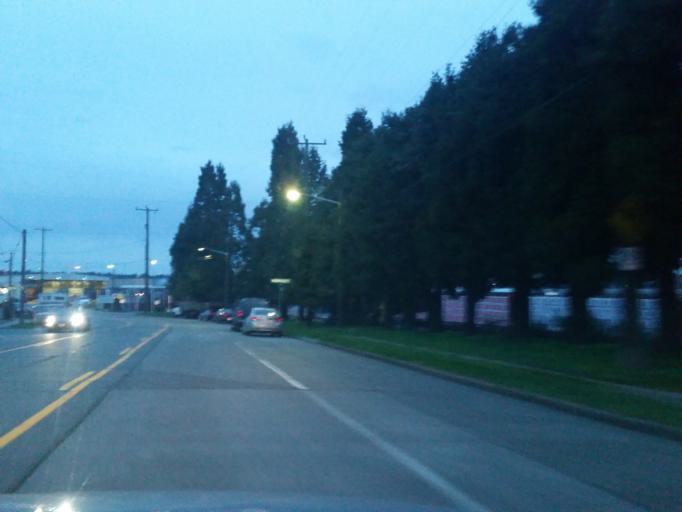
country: US
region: Washington
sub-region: King County
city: Seattle
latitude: 47.6499
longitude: -122.3820
